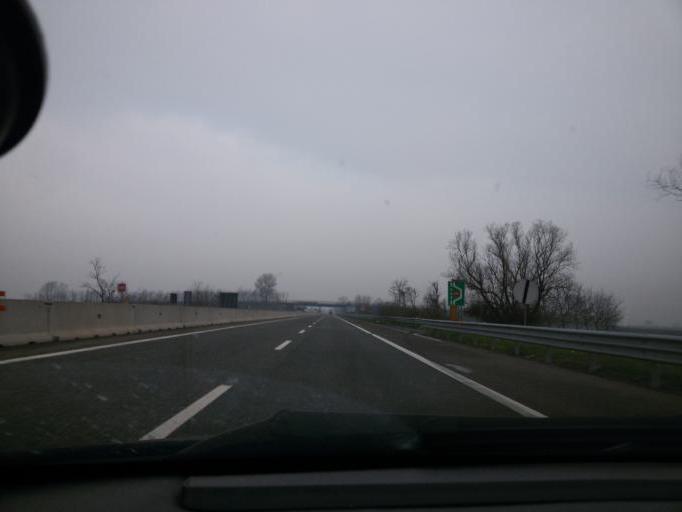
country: IT
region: Piedmont
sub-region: Provincia di Vercelli
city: Stroppiana
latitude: 45.2484
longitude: 8.4585
